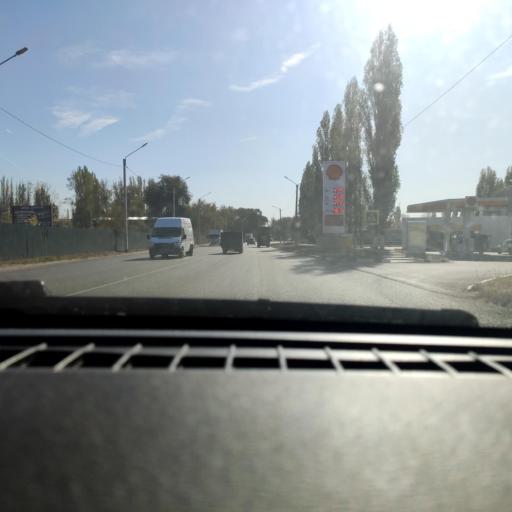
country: RU
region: Voronezj
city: Maslovka
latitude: 51.6280
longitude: 39.2617
